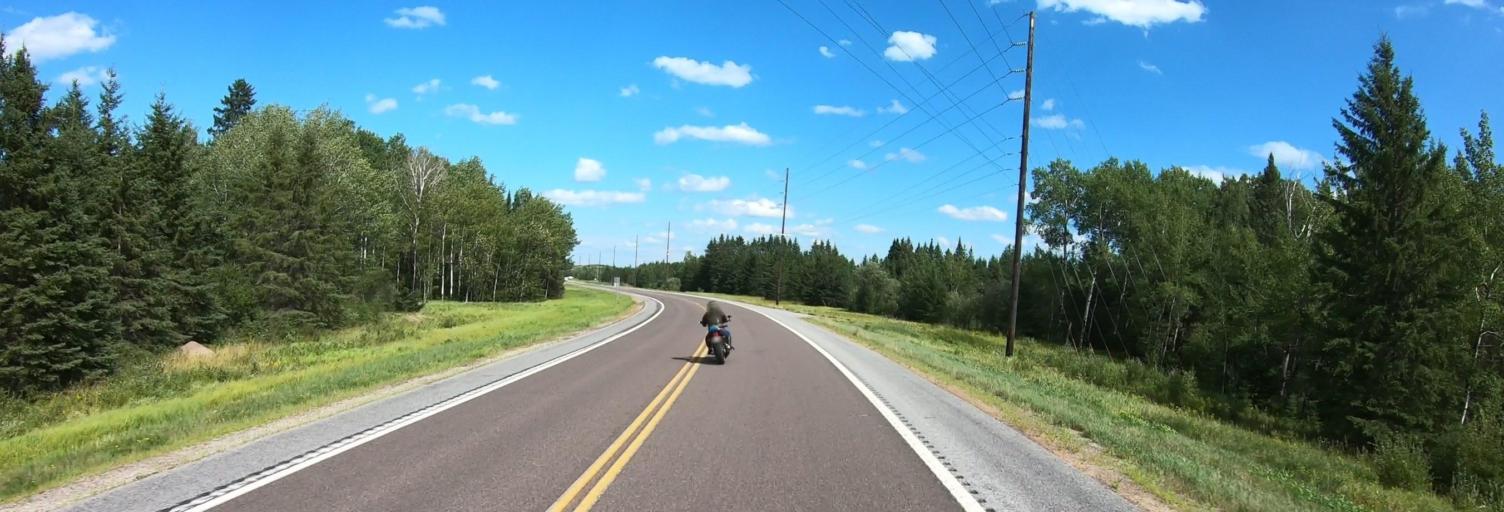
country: US
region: Minnesota
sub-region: Saint Louis County
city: Parkville
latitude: 47.8449
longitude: -92.5272
